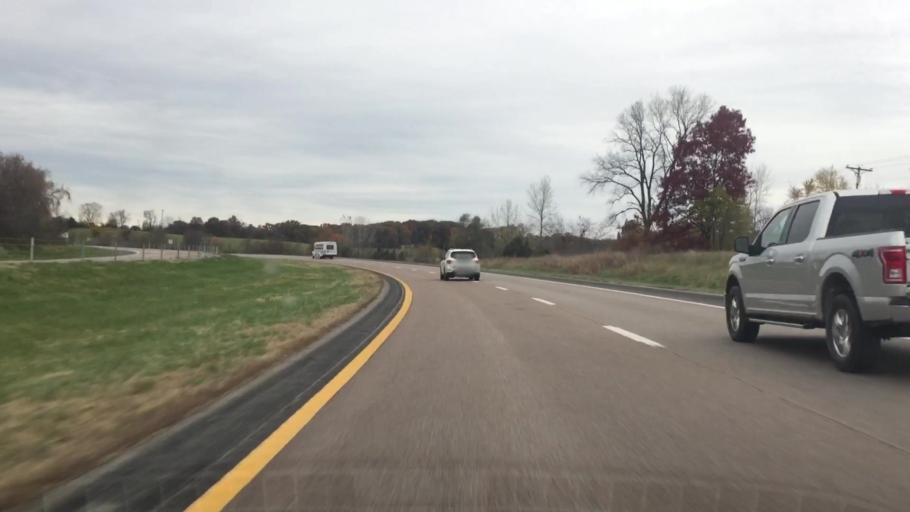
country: US
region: Missouri
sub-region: Cole County
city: Jefferson City
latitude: 38.6498
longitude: -92.2039
